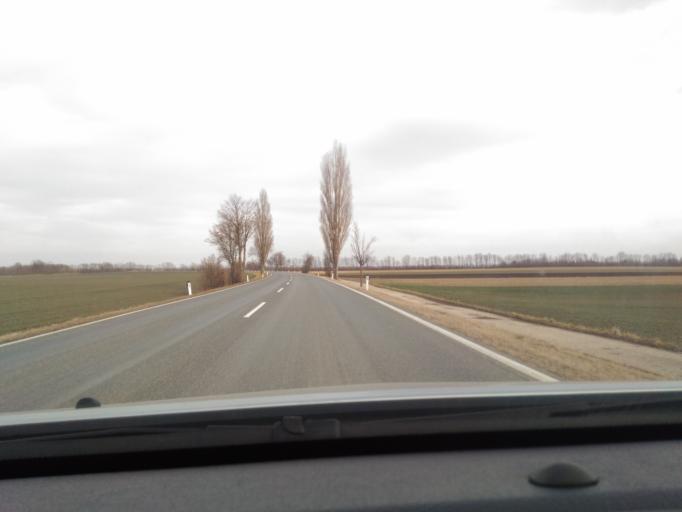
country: AT
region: Lower Austria
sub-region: Politischer Bezirk Hollabrunn
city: Mailberg
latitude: 48.7020
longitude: 16.2004
